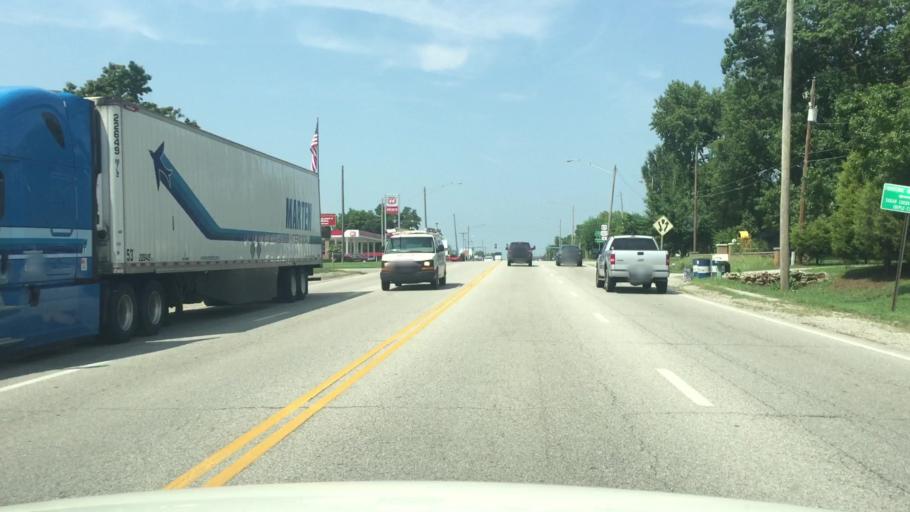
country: US
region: Kansas
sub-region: Crawford County
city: Frontenac
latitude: 37.4525
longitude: -94.7051
